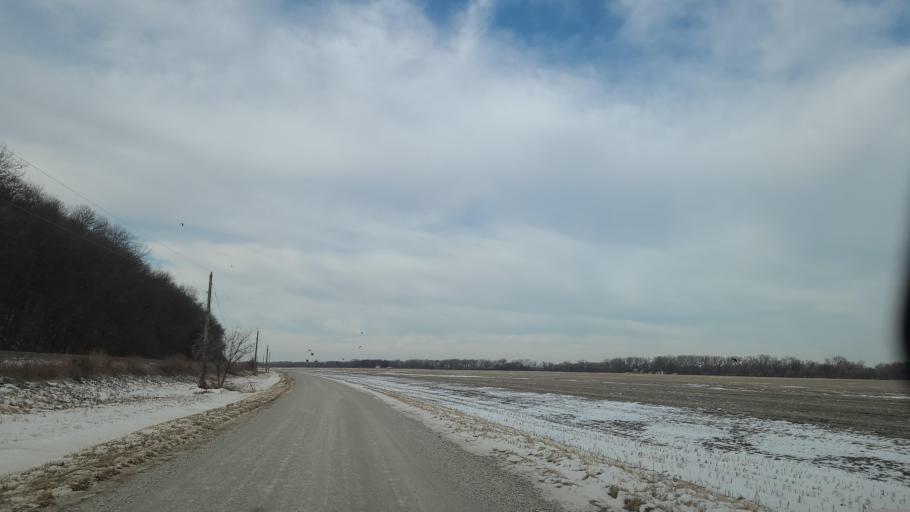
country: US
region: Kansas
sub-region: Jefferson County
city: Oskaloosa
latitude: 39.0614
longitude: -95.4282
